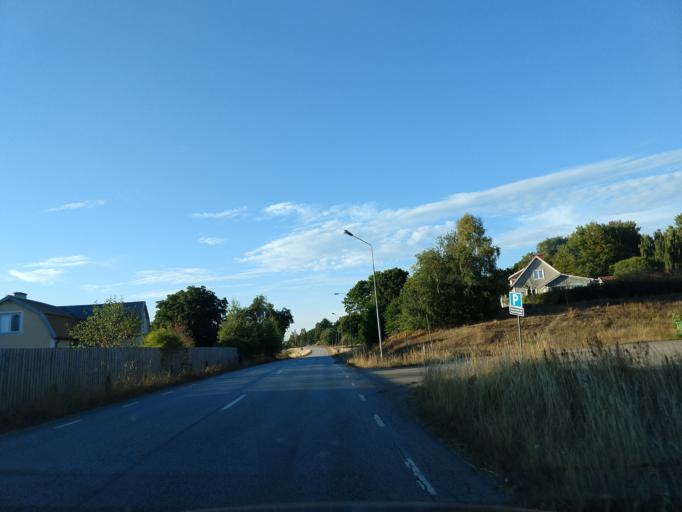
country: SE
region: Blekinge
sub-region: Ronneby Kommun
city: Brakne-Hoby
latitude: 56.2399
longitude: 15.1173
